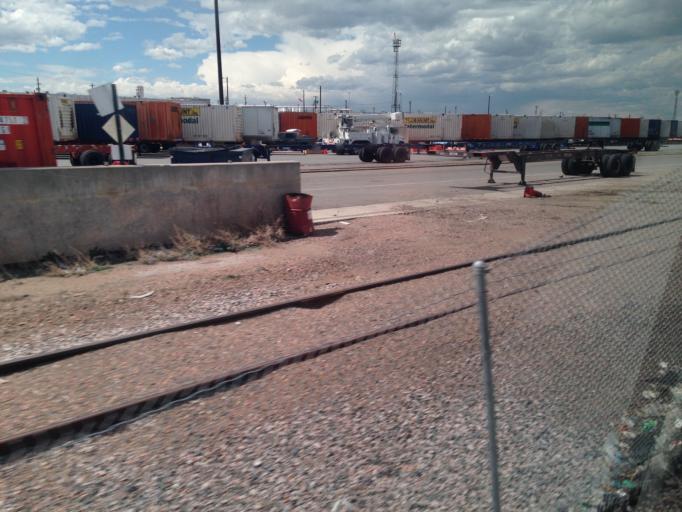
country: US
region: Colorado
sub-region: Adams County
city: Berkley
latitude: 39.7848
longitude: -104.9967
